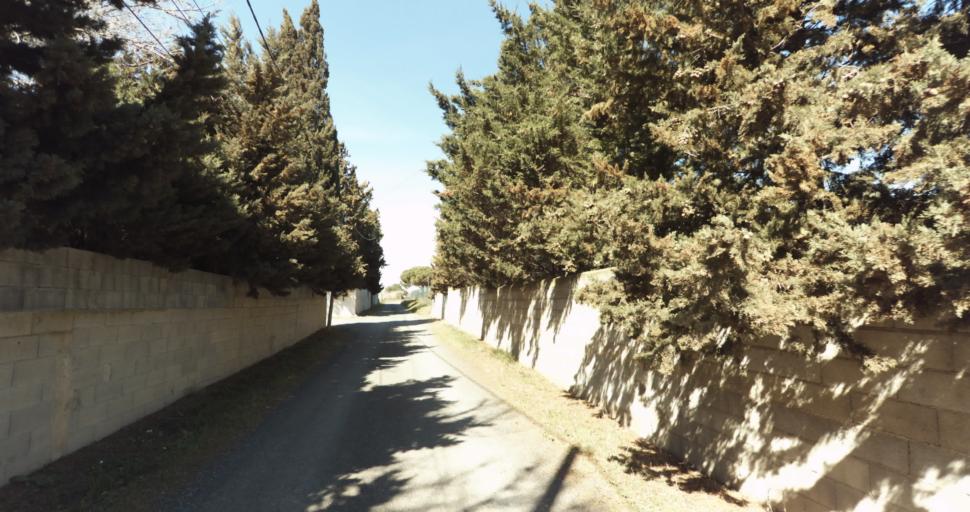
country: FR
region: Languedoc-Roussillon
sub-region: Departement de l'Herault
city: Marseillan
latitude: 43.3695
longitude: 3.5398
